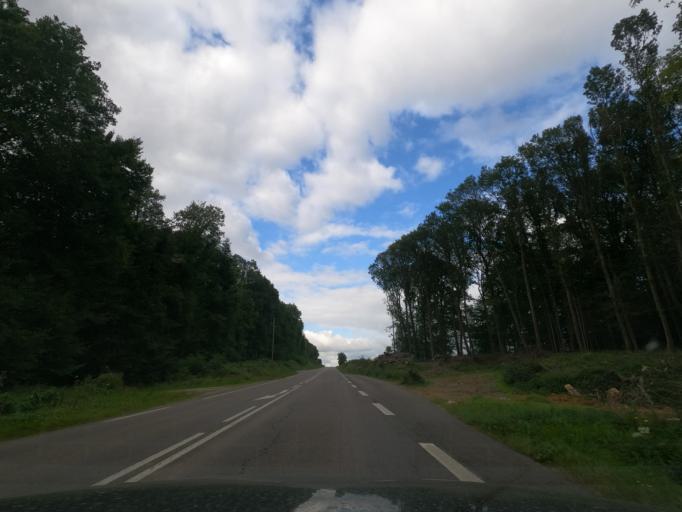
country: FR
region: Lower Normandy
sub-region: Departement de l'Orne
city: Gace
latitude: 48.8839
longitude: 0.3913
